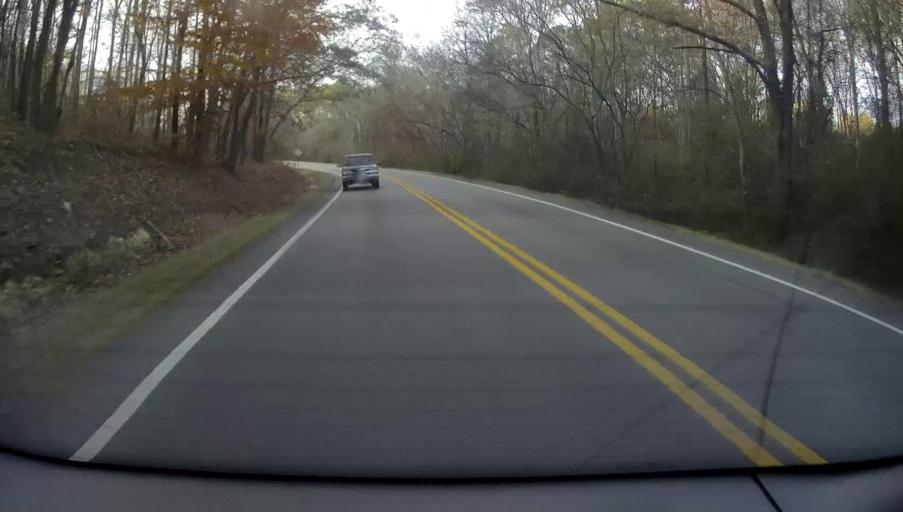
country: US
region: Alabama
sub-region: Etowah County
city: Attalla
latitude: 34.0385
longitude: -86.1136
